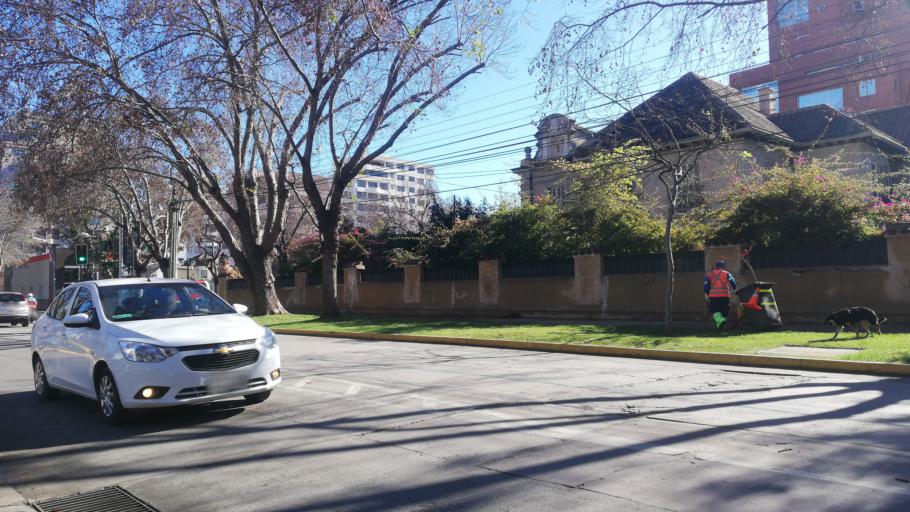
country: CL
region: Valparaiso
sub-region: Provincia de Valparaiso
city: Vina del Mar
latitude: -33.0154
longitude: -71.5493
